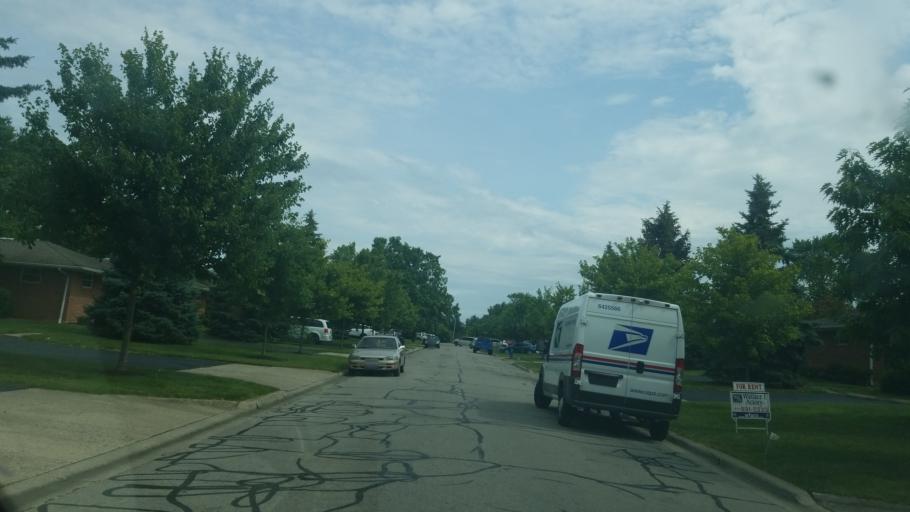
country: US
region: Ohio
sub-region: Franklin County
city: Worthington
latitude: 40.0952
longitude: -83.0051
